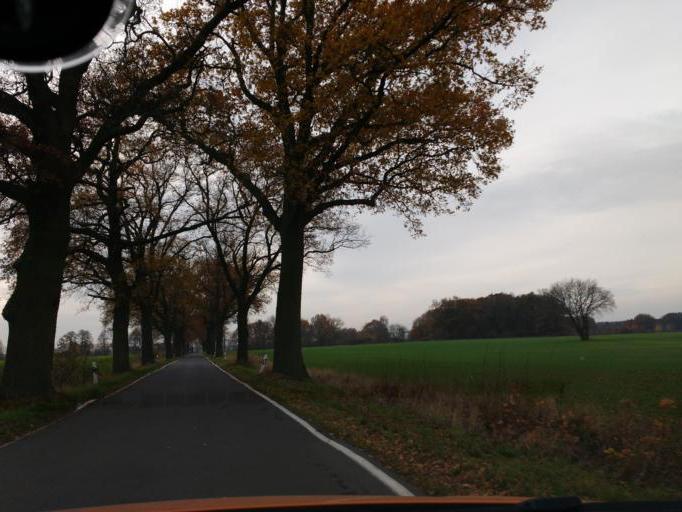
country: DE
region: Brandenburg
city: Kremmen
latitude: 52.7307
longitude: 13.0677
